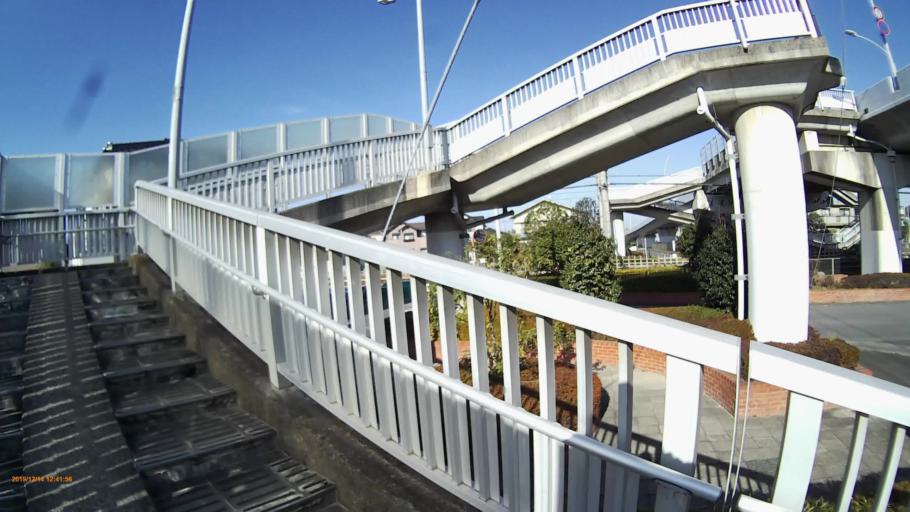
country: JP
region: Saitama
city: Fukiage-fujimi
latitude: 36.1047
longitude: 139.4476
